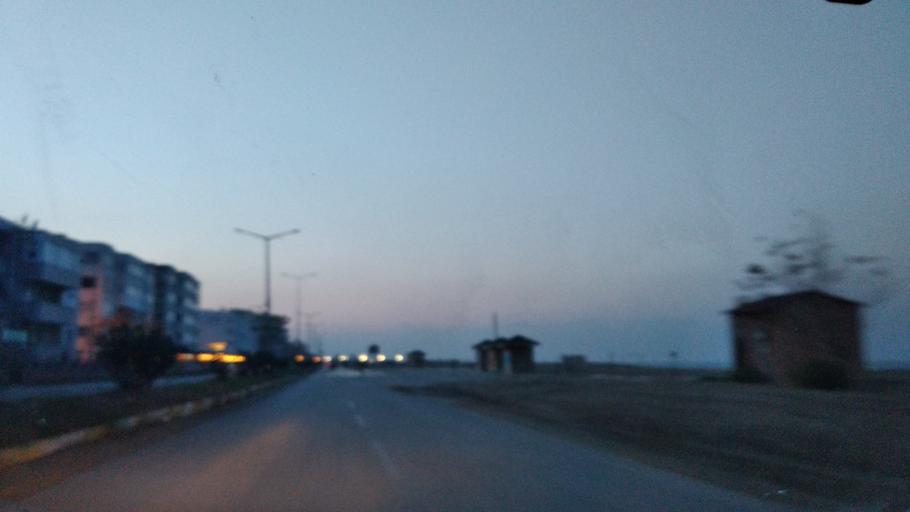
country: TR
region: Sakarya
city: Karasu
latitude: 41.1007
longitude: 30.7185
